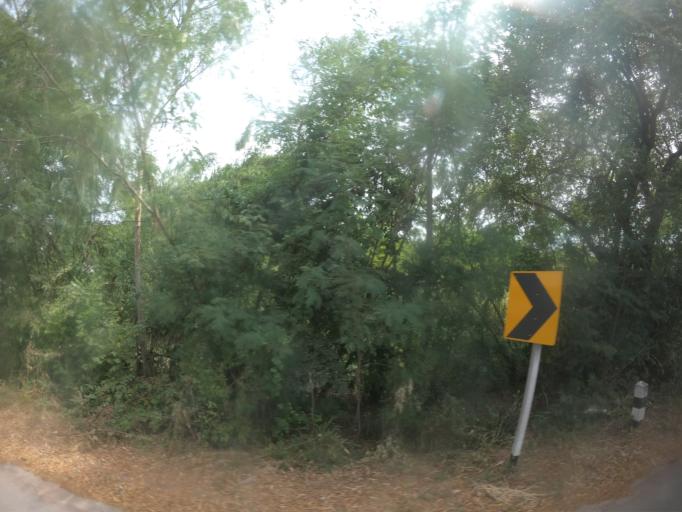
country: TH
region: Maha Sarakham
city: Chiang Yuen
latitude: 16.3697
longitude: 103.1062
